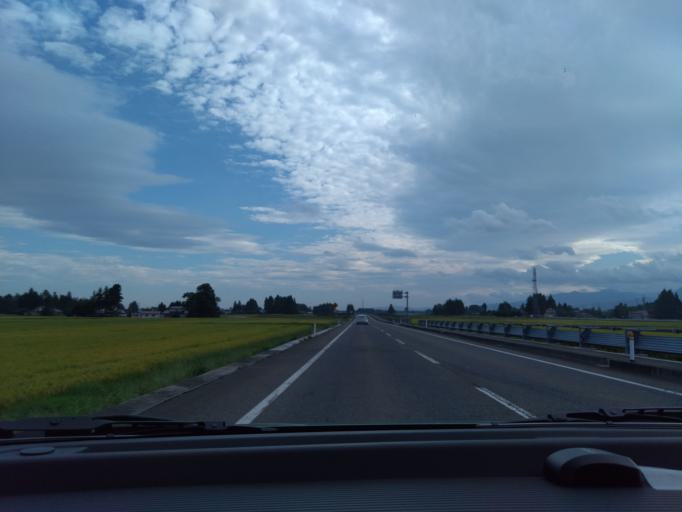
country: JP
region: Iwate
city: Hanamaki
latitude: 39.3552
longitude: 141.0544
